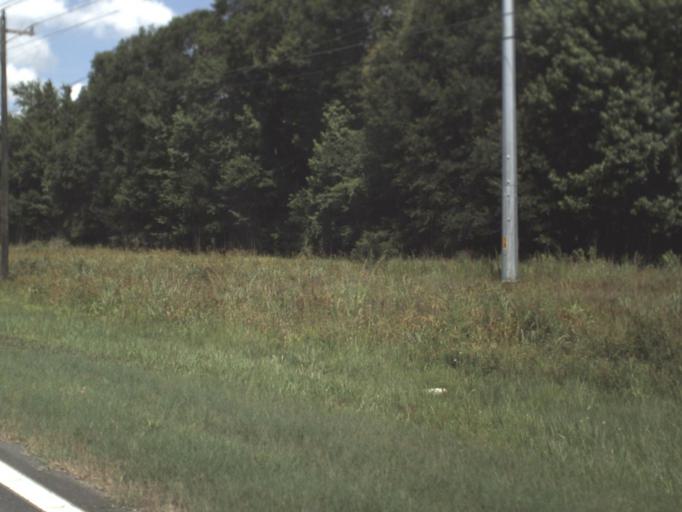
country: US
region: Florida
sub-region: Levy County
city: Chiefland
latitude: 29.2794
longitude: -82.8539
